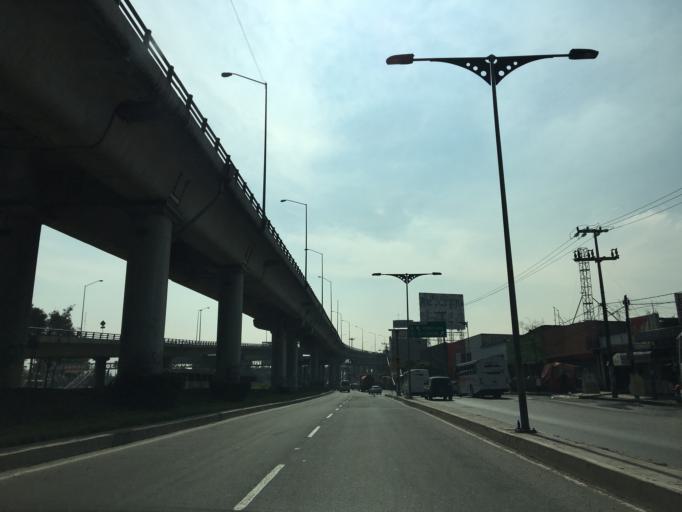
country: MX
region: Mexico
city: Los Reyes La Paz
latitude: 19.3616
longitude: -99.0020
